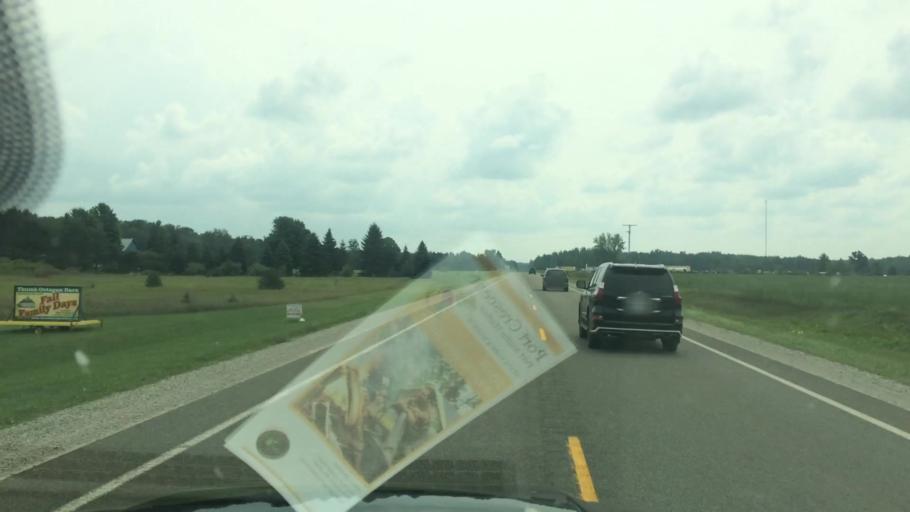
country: US
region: Michigan
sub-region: Tuscola County
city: Cass City
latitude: 43.6700
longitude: -83.0983
